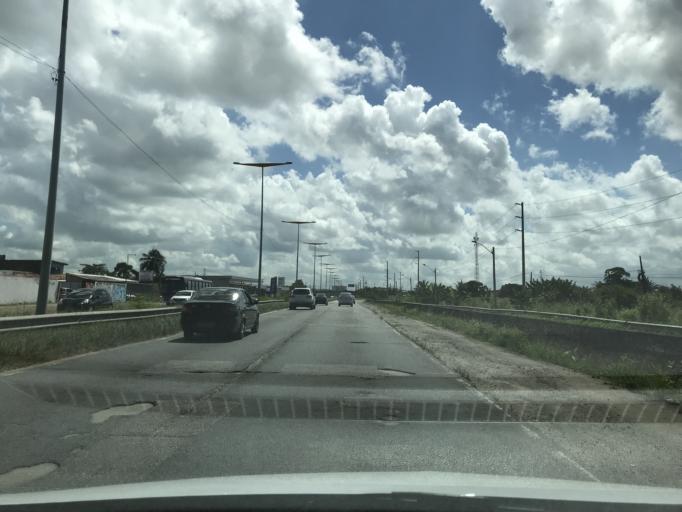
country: BR
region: Pernambuco
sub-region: Recife
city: Recife
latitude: -8.0738
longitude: -34.9373
